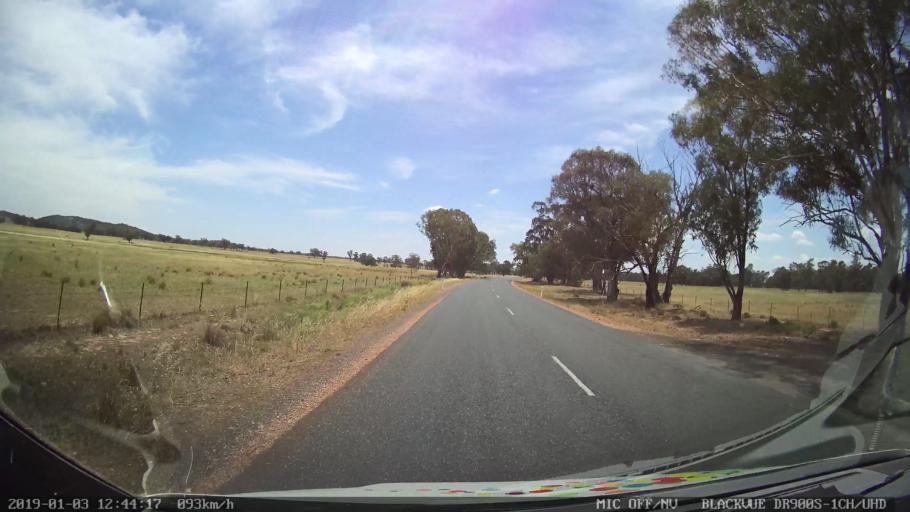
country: AU
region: New South Wales
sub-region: Weddin
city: Grenfell
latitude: -33.7636
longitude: 148.2151
